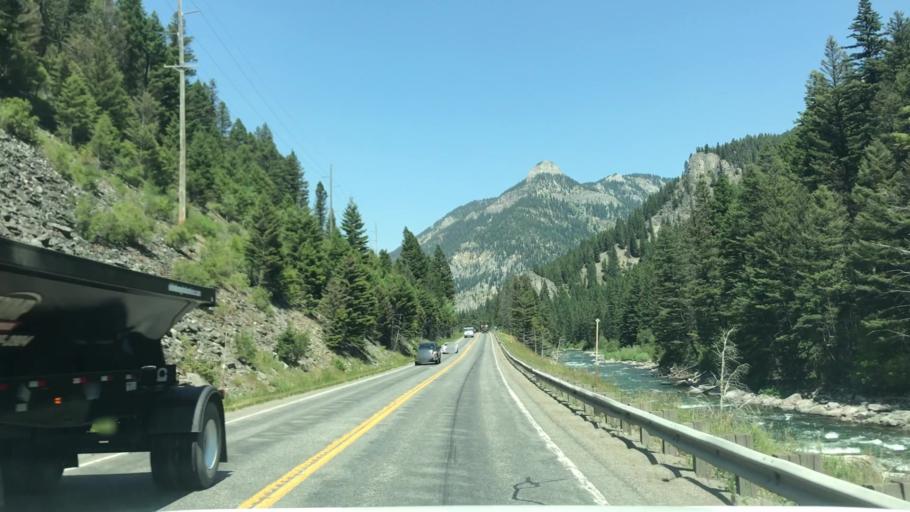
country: US
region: Montana
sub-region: Gallatin County
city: Big Sky
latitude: 45.4244
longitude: -111.2340
